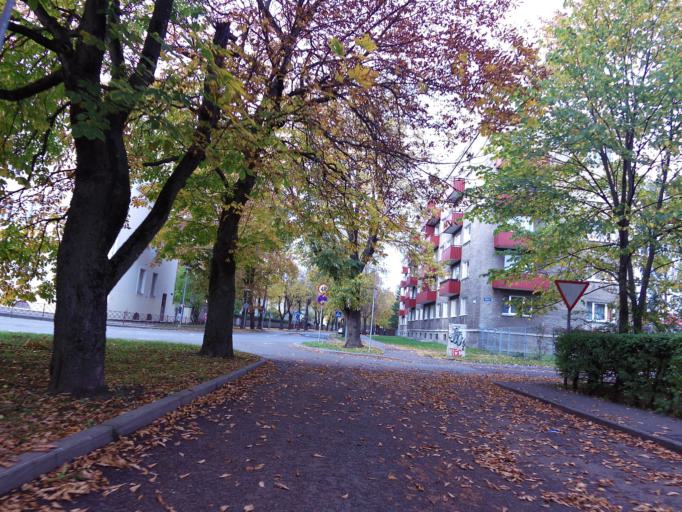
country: EE
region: Harju
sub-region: Tallinna linn
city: Tallinn
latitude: 59.4420
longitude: 24.7135
